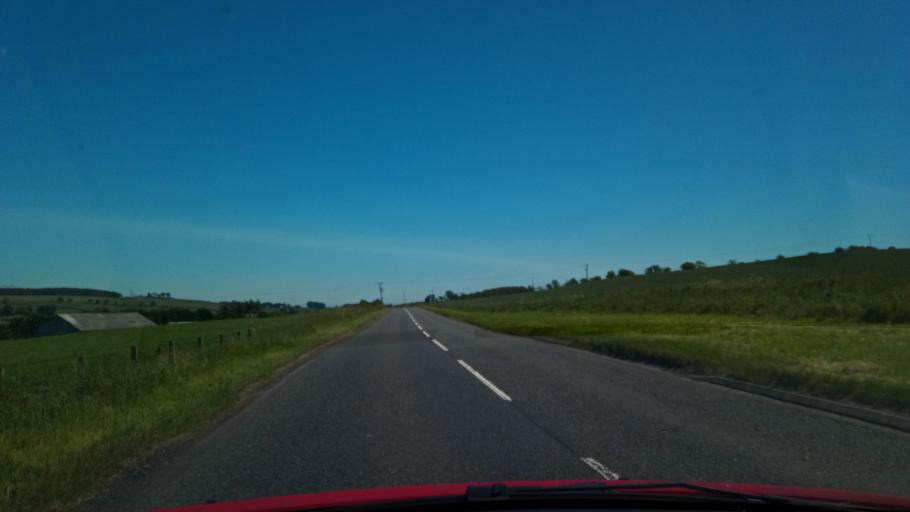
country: GB
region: Scotland
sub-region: The Scottish Borders
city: Kelso
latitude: 55.7006
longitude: -2.4701
